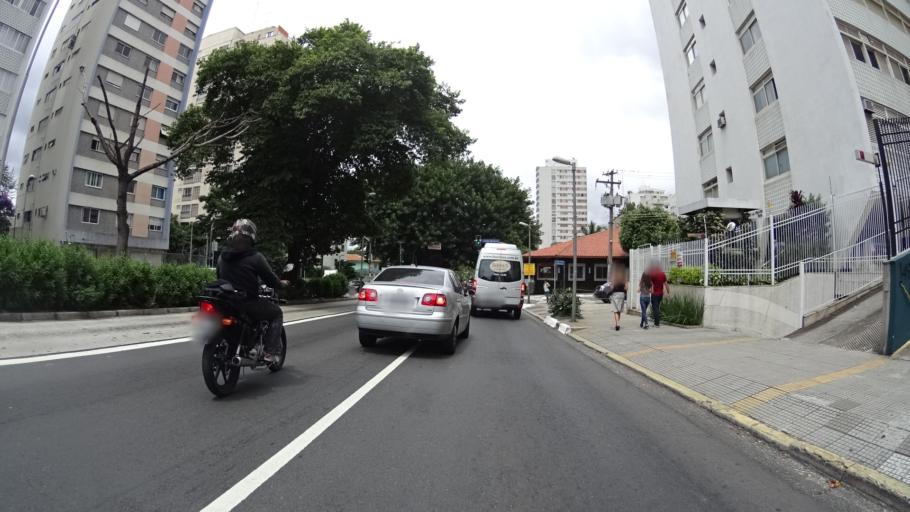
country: BR
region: Sao Paulo
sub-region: Sao Paulo
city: Sao Paulo
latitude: -23.5627
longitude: -46.6756
